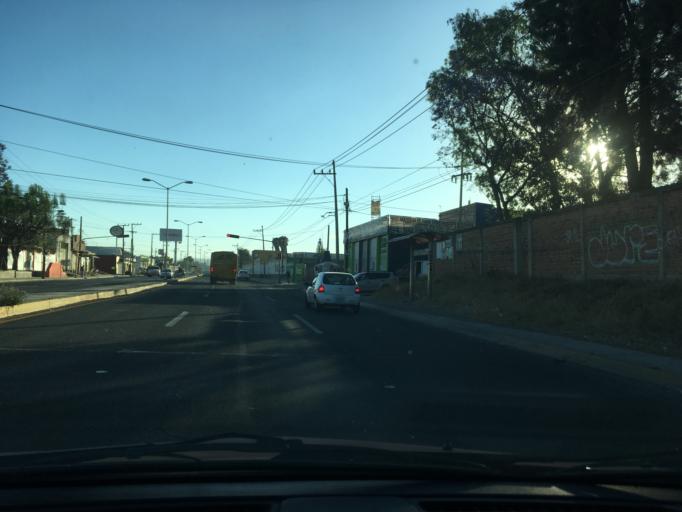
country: MX
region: Jalisco
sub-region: Tlajomulco de Zuniga
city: La Tijera
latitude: 20.5889
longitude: -103.4180
